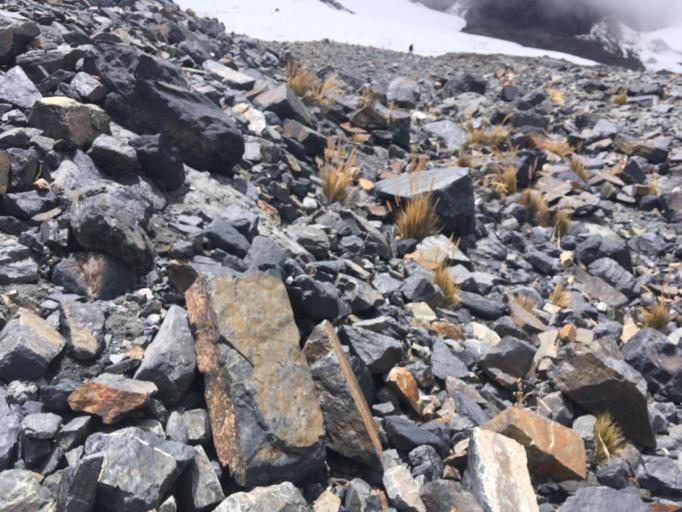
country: BO
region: La Paz
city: La Paz
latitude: -16.3986
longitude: -67.9452
